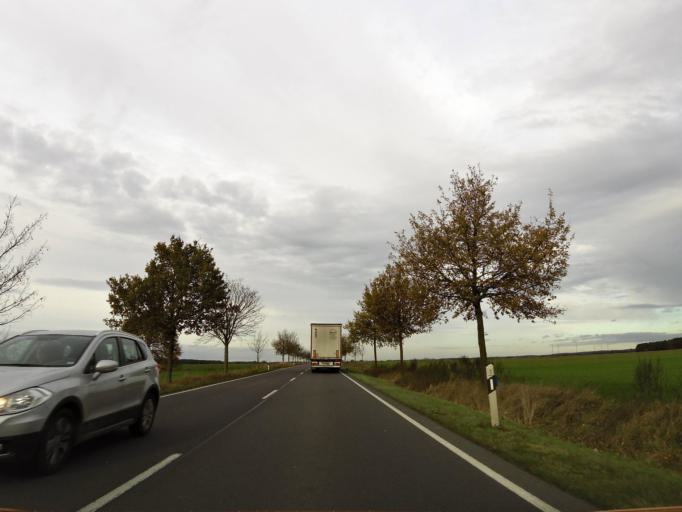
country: DE
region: Saxony-Anhalt
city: Pretzier
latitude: 52.7209
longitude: 11.2485
